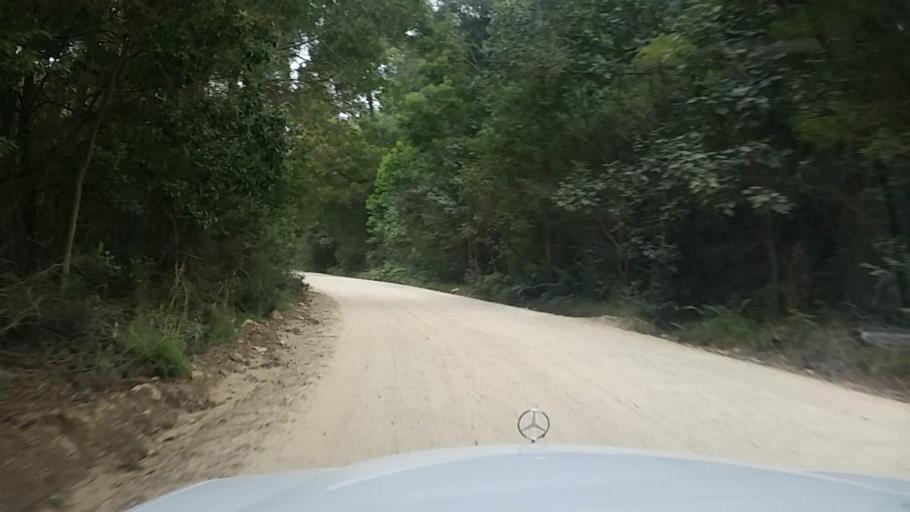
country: ZA
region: Western Cape
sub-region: Eden District Municipality
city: Knysna
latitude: -33.9749
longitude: 23.1436
